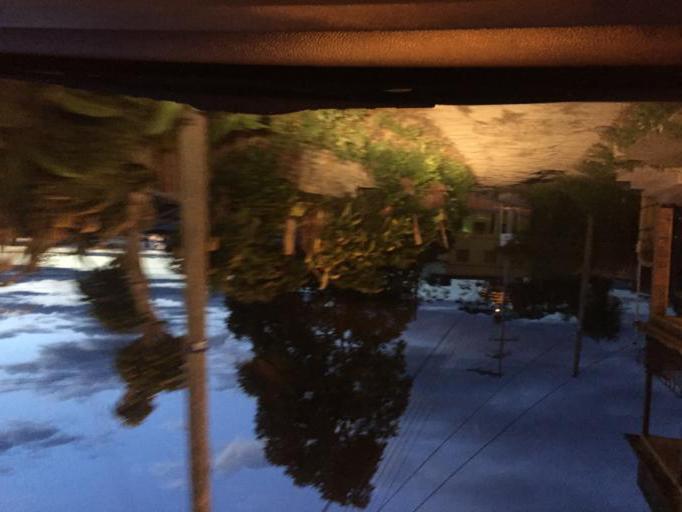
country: CO
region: Cundinamarca
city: Zipacon
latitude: 4.7195
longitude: -74.4276
